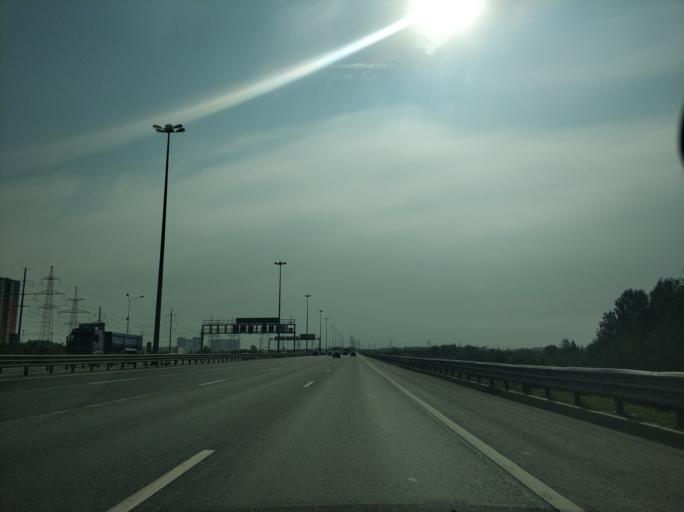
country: RU
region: Leningrad
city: Murino
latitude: 60.0277
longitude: 30.4476
